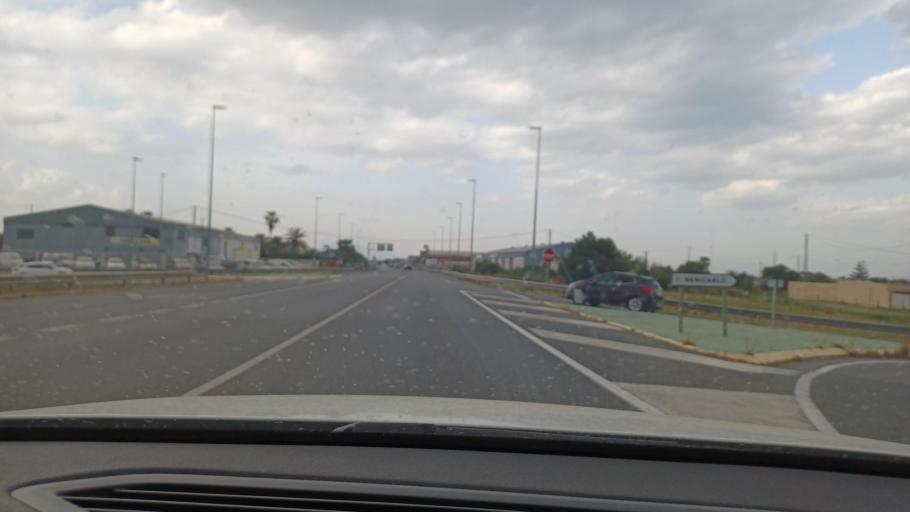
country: ES
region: Valencia
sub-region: Provincia de Castello
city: Benicarlo
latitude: 40.4320
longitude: 0.4374
